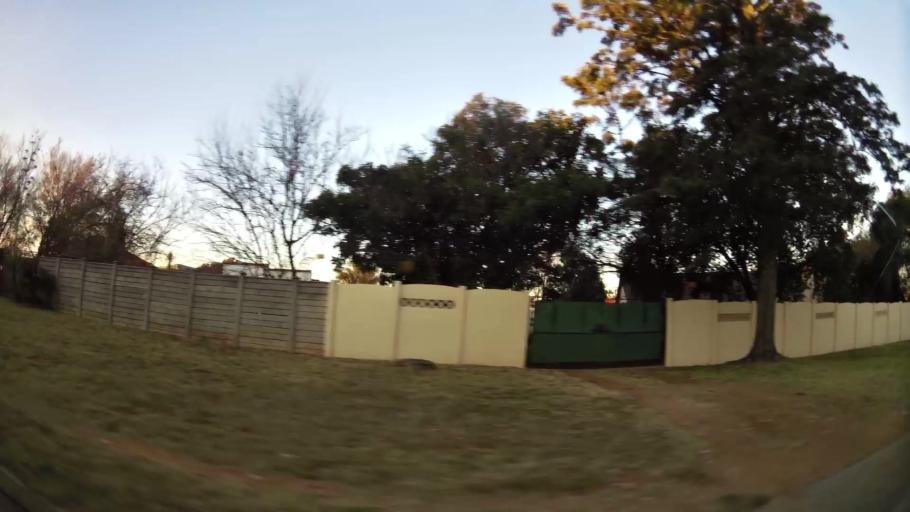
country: ZA
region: Gauteng
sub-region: City of Johannesburg Metropolitan Municipality
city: Roodepoort
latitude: -26.1507
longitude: 27.8818
